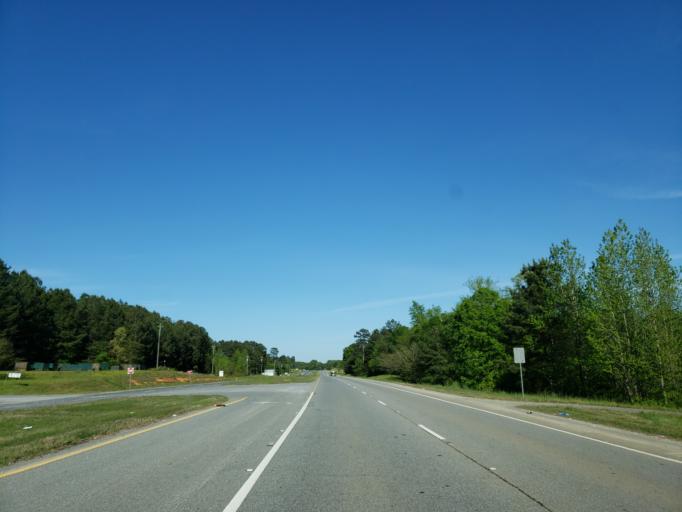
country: US
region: Georgia
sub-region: Polk County
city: Cedartown
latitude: 34.0037
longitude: -85.1631
